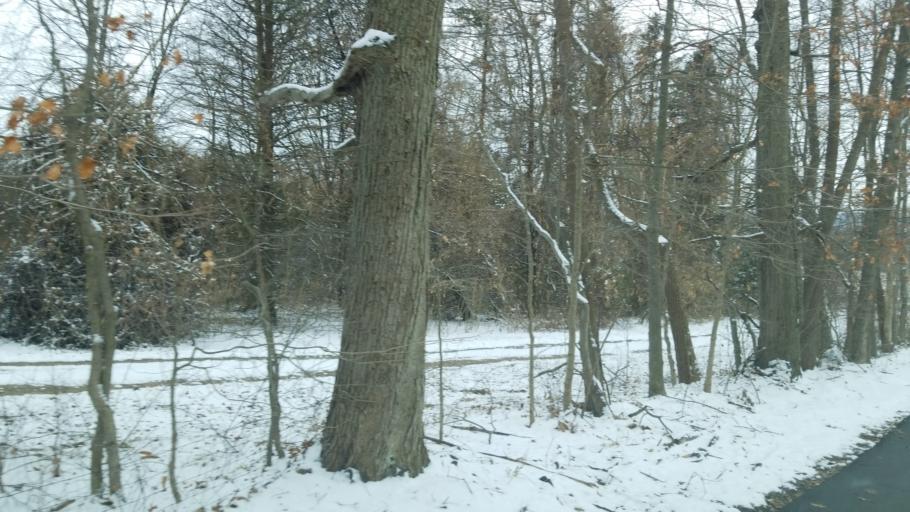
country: US
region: Ohio
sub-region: Richland County
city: Lexington
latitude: 40.6886
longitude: -82.5630
